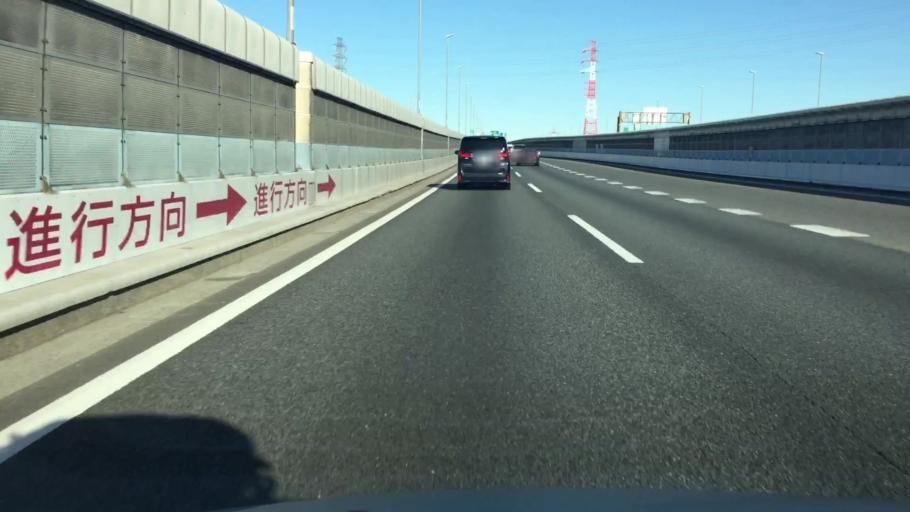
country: JP
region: Saitama
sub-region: Kawaguchi-shi
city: Hatogaya-honcho
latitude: 35.8263
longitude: 139.7588
